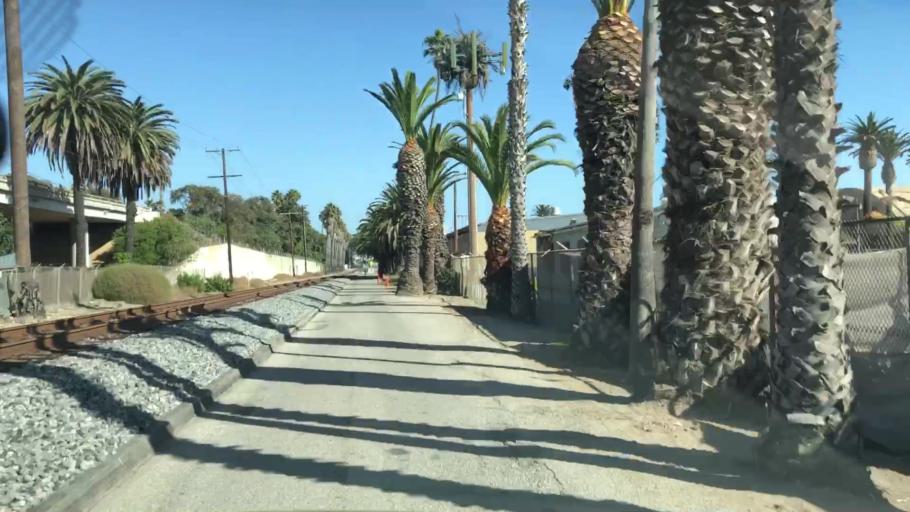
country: US
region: California
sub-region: Ventura County
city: Ventura
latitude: 34.2769
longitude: -119.3031
